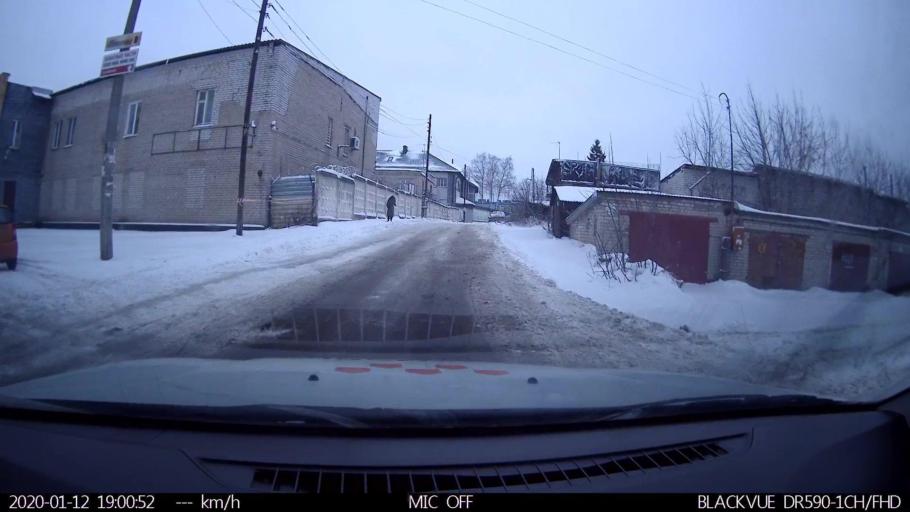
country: RU
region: Nizjnij Novgorod
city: Nizhniy Novgorod
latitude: 56.3307
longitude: 43.9104
